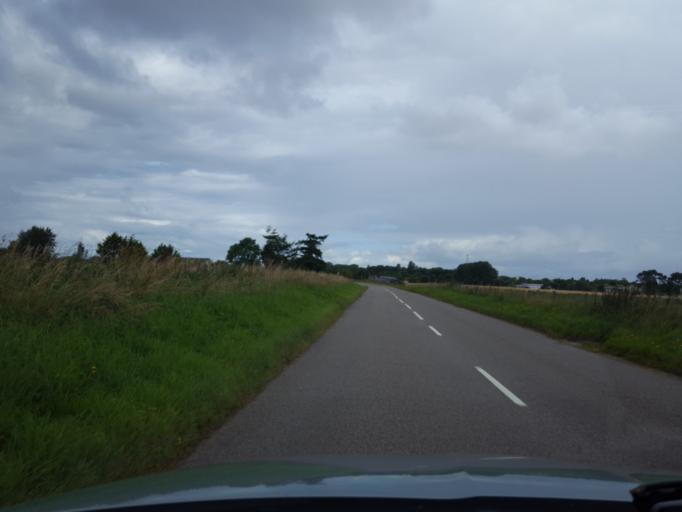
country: GB
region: Scotland
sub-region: Moray
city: Kinloss
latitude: 57.6284
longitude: -3.5490
